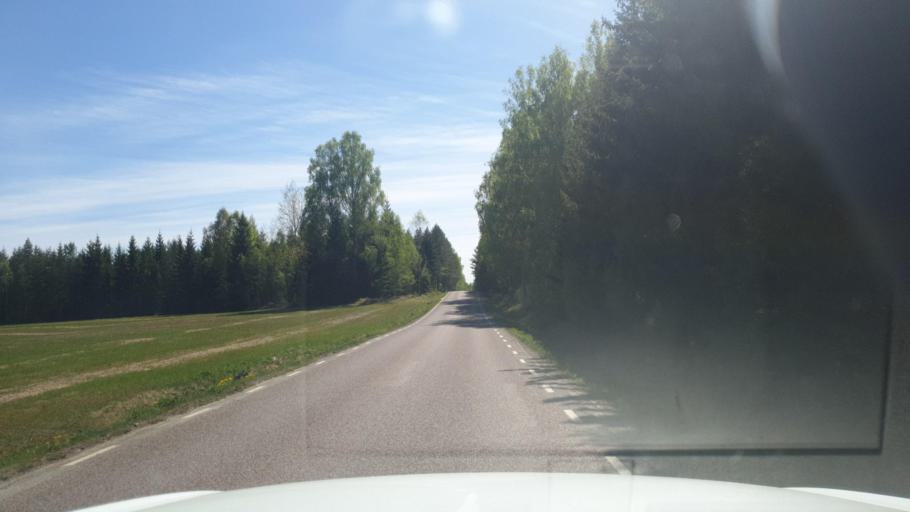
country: SE
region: Vaermland
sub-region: Karlstads Kommun
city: Edsvalla
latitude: 59.5133
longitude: 13.1103
